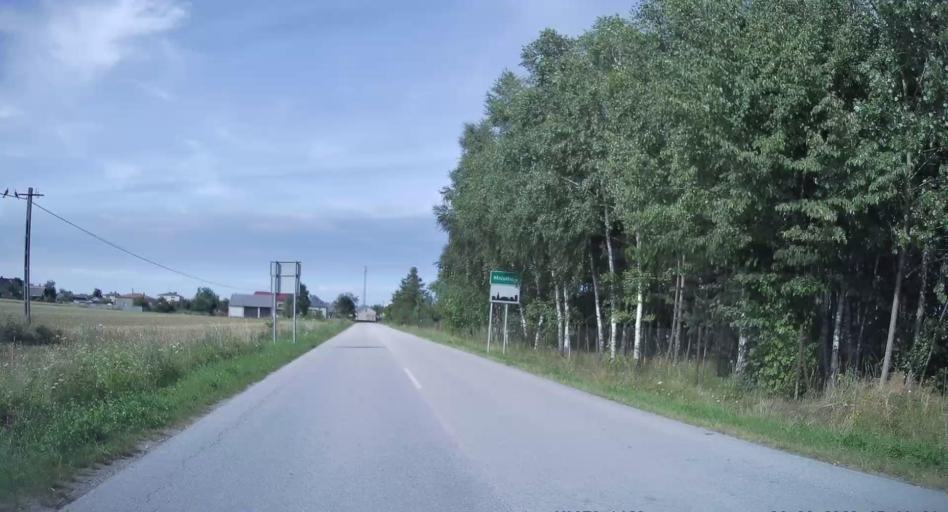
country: PL
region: Lodz Voivodeship
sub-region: Powiat opoczynski
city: Mniszkow
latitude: 51.3679
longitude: 20.0389
